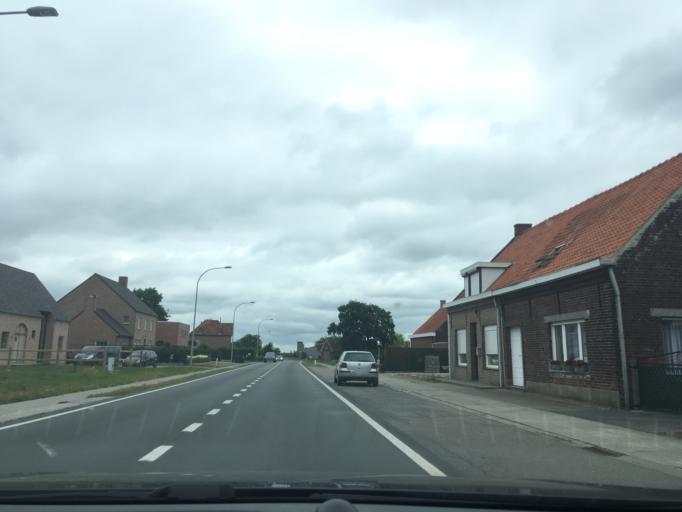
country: BE
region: Flanders
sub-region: Provincie West-Vlaanderen
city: Tielt
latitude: 51.0320
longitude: 3.3042
